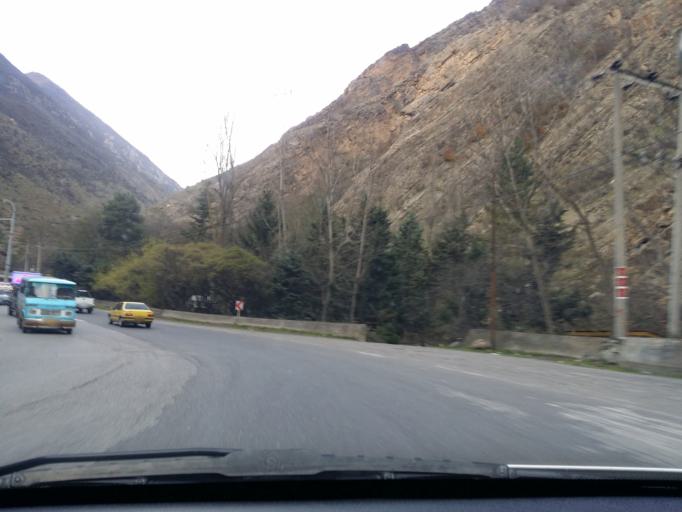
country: IR
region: Mazandaran
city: Chalus
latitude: 36.3177
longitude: 51.2478
